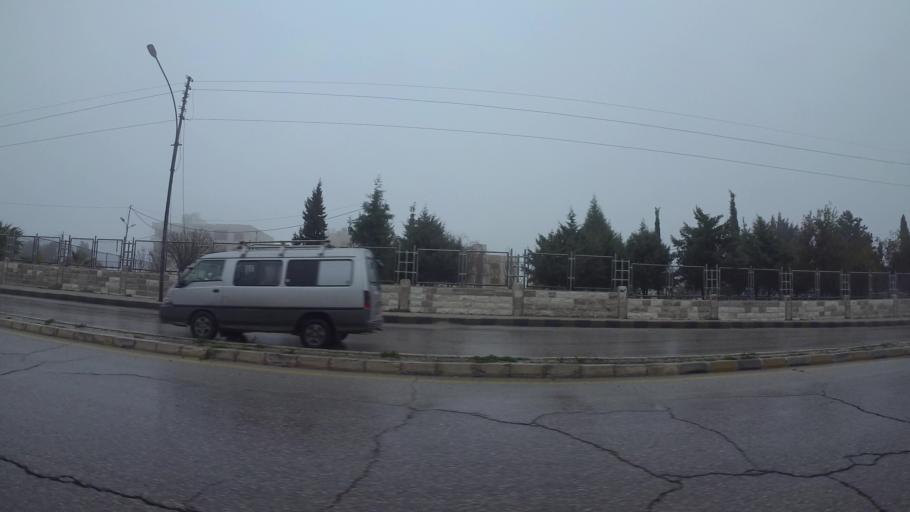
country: JO
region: Amman
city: Al Jubayhah
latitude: 32.0291
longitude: 35.8304
